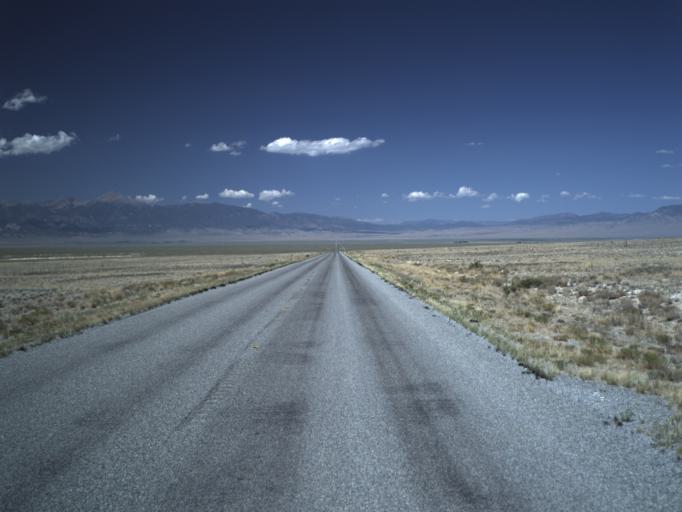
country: US
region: Nevada
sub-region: White Pine County
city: McGill
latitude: 39.0408
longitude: -113.8358
